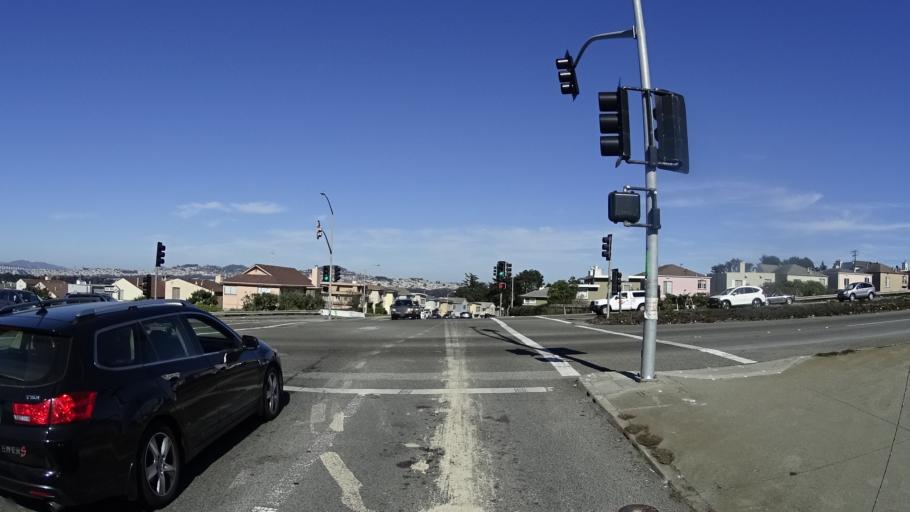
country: US
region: California
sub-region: San Mateo County
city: Broadmoor
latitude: 37.6904
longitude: -122.4929
